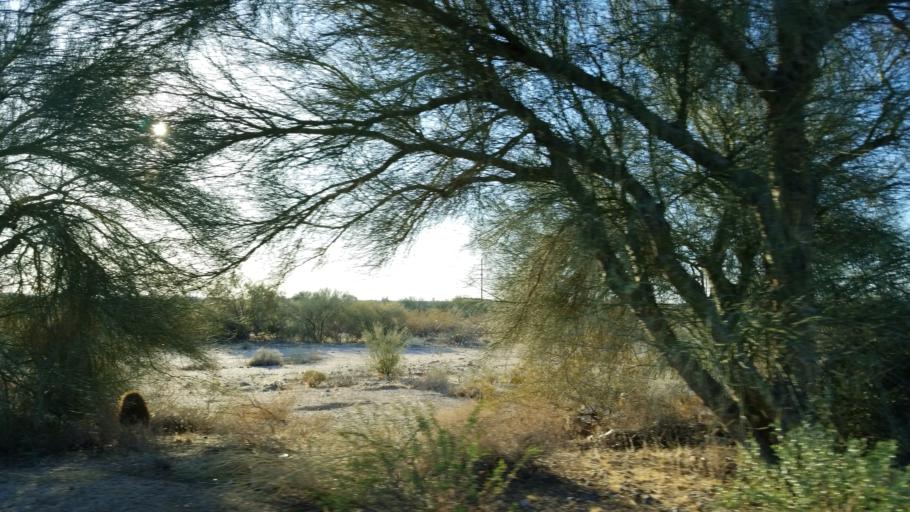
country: US
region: Arizona
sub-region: Maricopa County
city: Paradise Valley
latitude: 33.6471
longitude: -111.8854
